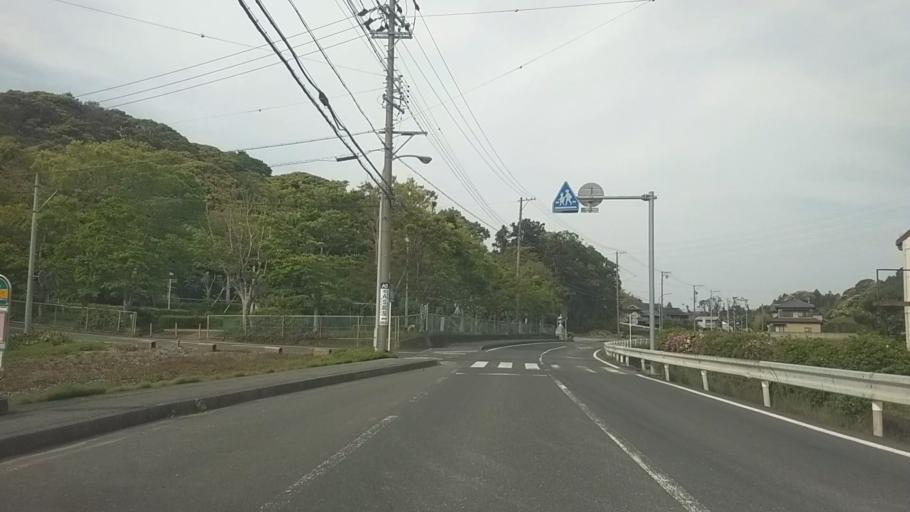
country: JP
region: Shizuoka
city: Hamamatsu
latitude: 34.7181
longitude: 137.6529
